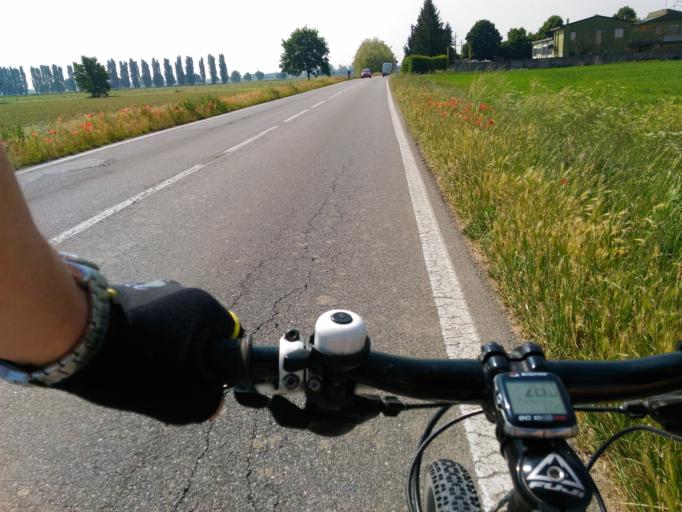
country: IT
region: Lombardy
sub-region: Provincia di Lodi
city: Salerano sul Lambro
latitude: 45.2761
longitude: 9.3827
